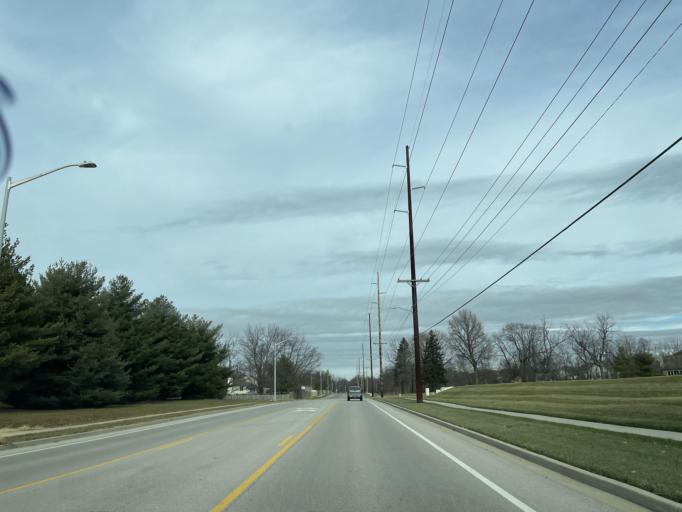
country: US
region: Illinois
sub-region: Sangamon County
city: Jerome
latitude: 39.7733
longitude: -89.7346
